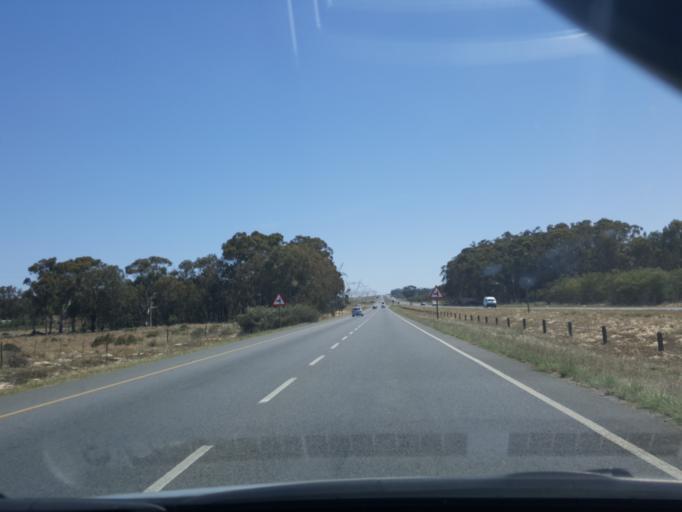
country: ZA
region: Western Cape
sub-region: City of Cape Town
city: Sunset Beach
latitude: -33.7537
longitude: 18.5466
